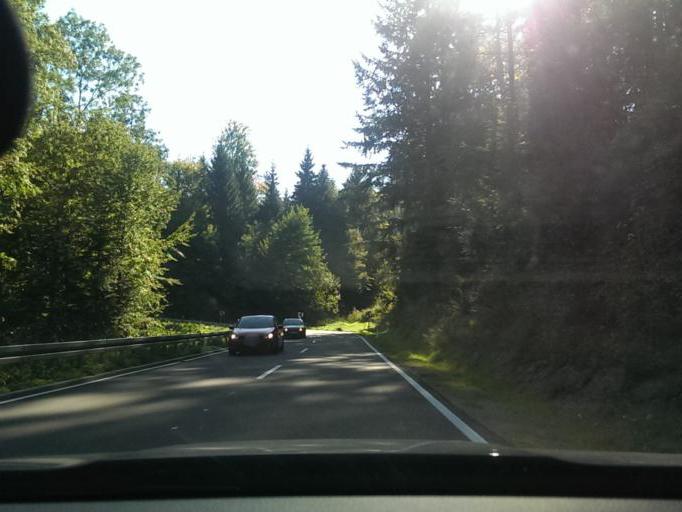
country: DE
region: Baden-Wuerttemberg
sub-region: Karlsruhe Region
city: Bad Herrenalb
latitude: 48.7997
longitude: 8.4679
